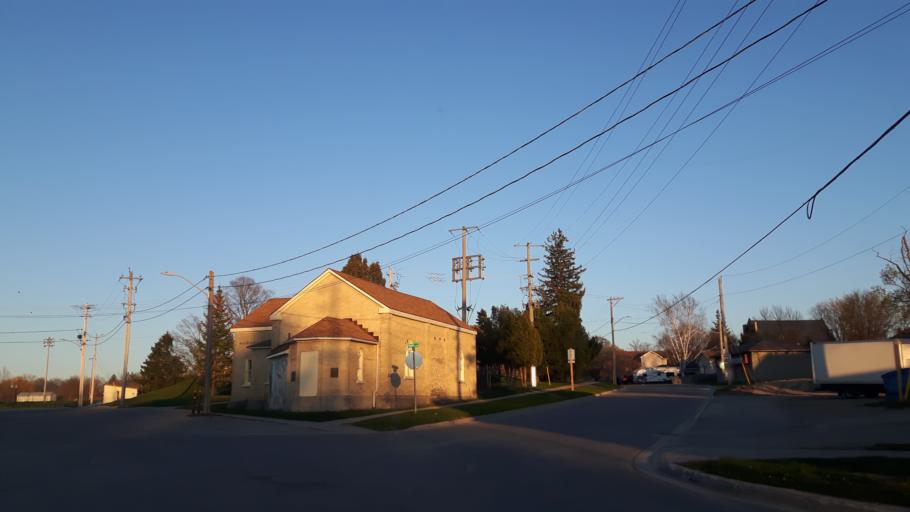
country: CA
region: Ontario
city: Bluewater
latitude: 43.6194
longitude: -81.5394
